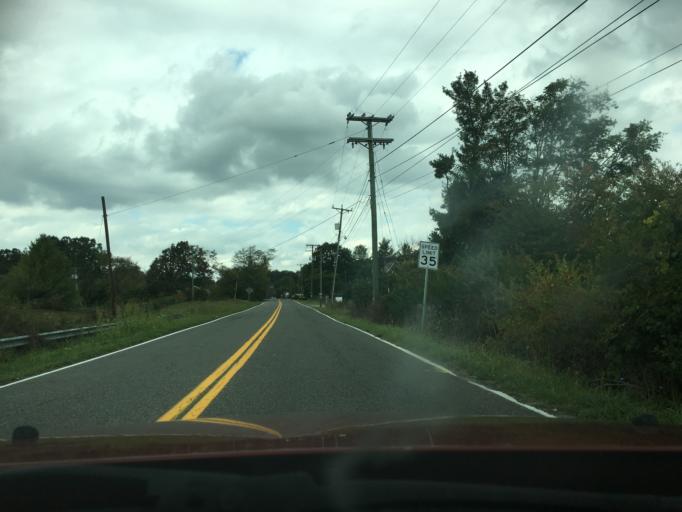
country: US
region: Virginia
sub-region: Pulaski County
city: Fairlawn
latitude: 37.1512
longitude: -80.5817
